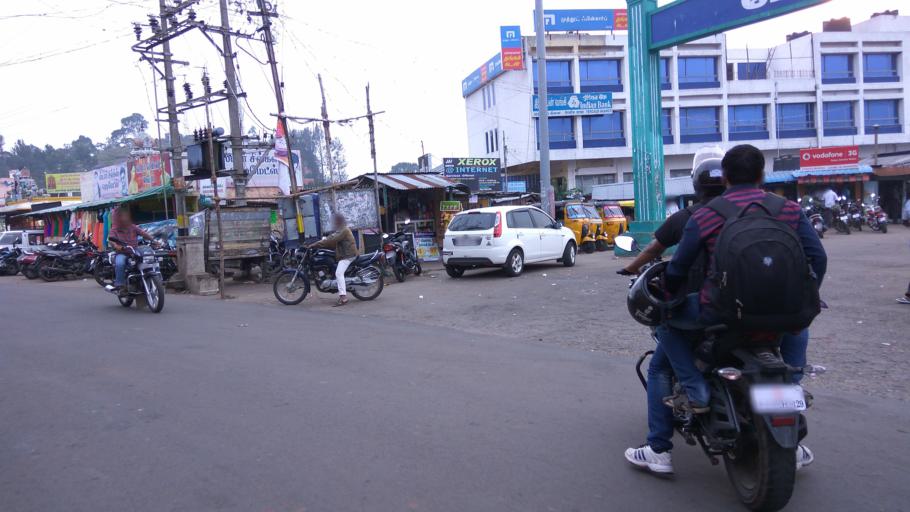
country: IN
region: Tamil Nadu
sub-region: Salem
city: Salem
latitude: 11.7765
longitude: 78.2092
